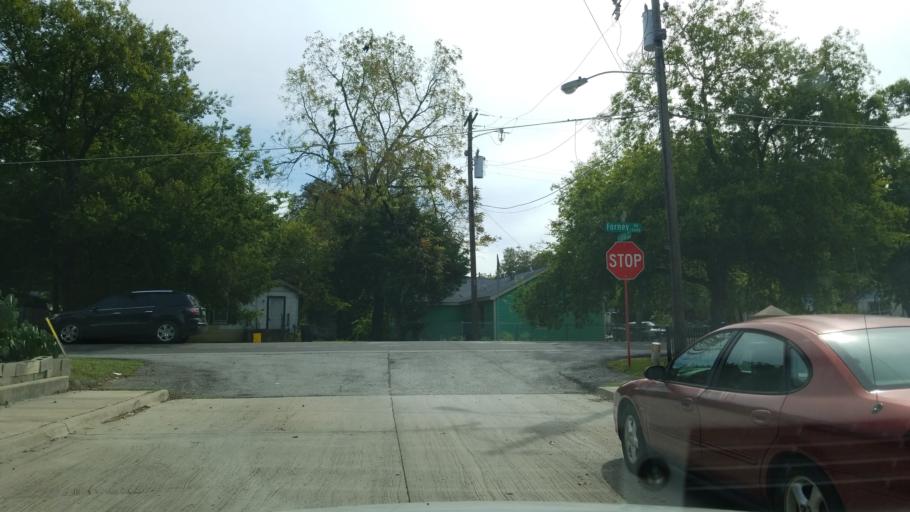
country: US
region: Texas
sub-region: Dallas County
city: Highland Park
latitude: 32.7853
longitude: -96.7205
